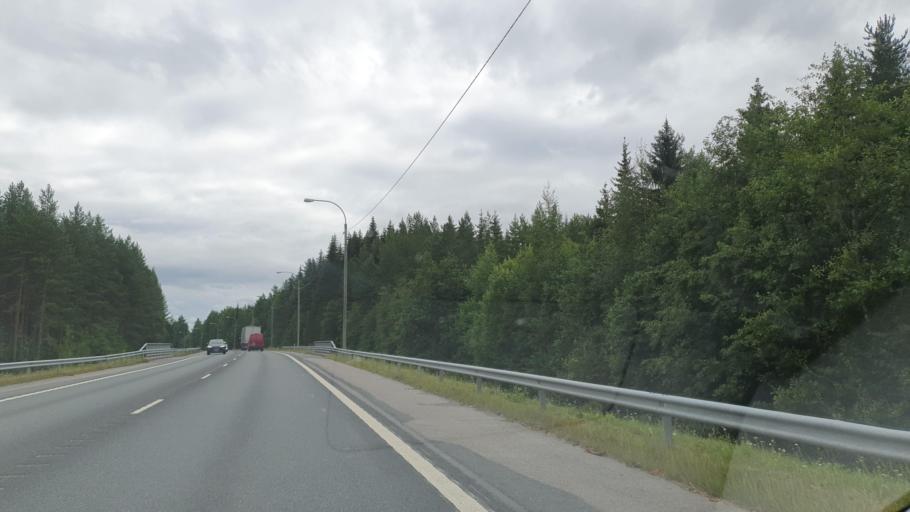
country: FI
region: Northern Savo
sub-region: Ylae-Savo
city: Iisalmi
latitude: 63.5115
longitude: 27.2567
